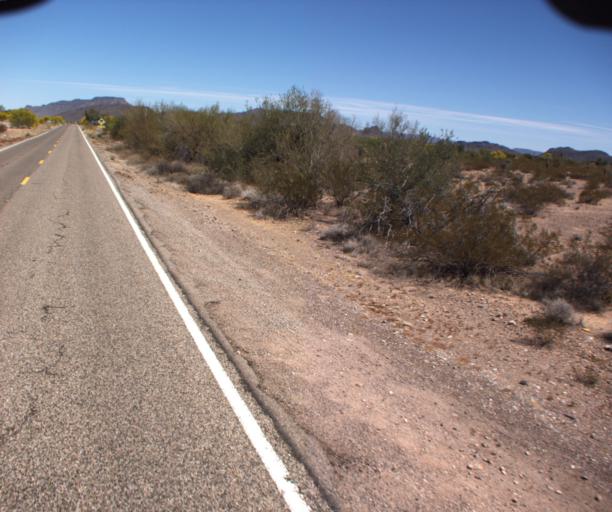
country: US
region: Arizona
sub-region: Pima County
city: Ajo
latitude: 32.2362
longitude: -112.7513
